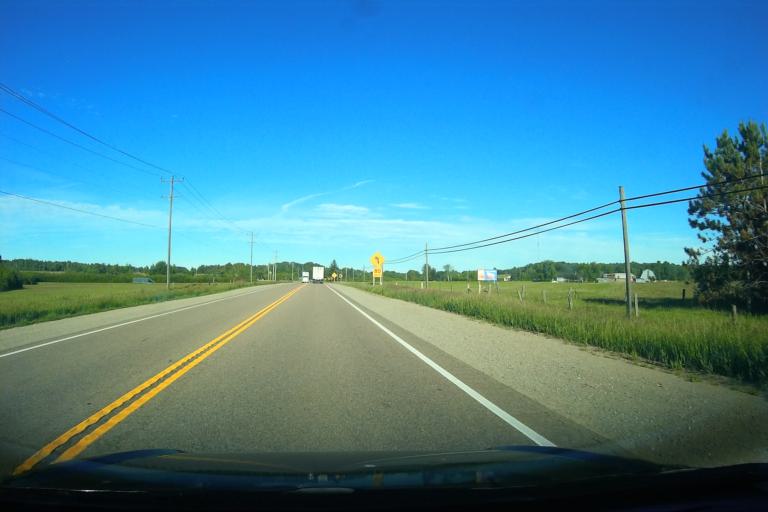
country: CA
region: Ontario
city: Renfrew
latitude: 45.5706
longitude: -76.7997
